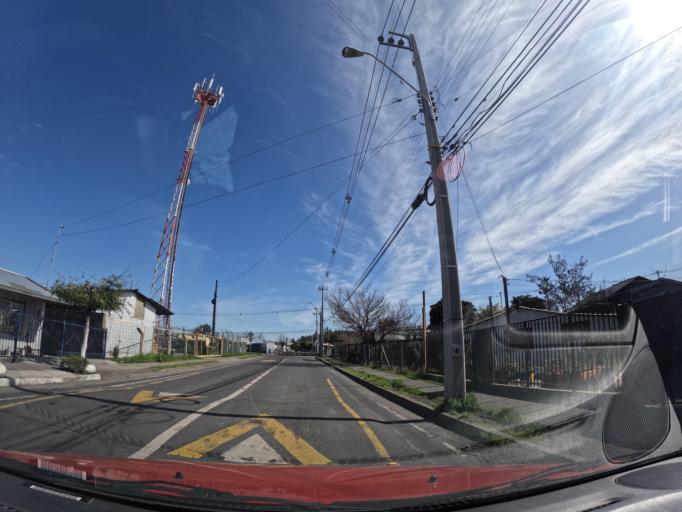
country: CL
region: Biobio
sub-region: Provincia de Biobio
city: Cabrero
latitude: -37.0798
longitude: -72.4393
